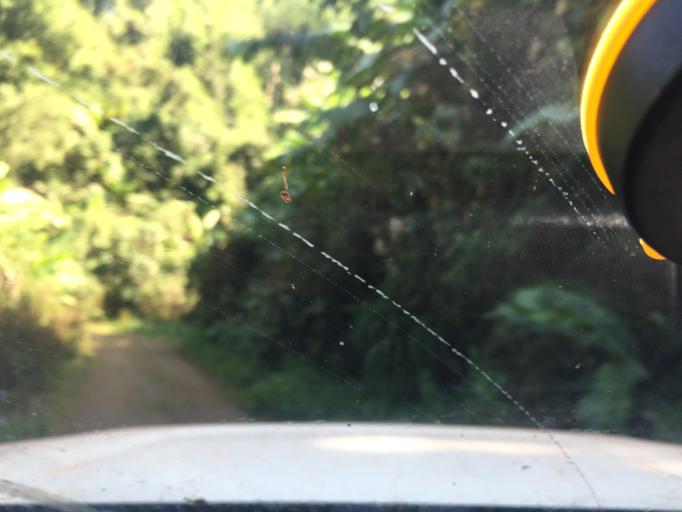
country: LA
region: Phongsali
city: Phongsali
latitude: 21.7007
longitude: 102.3939
